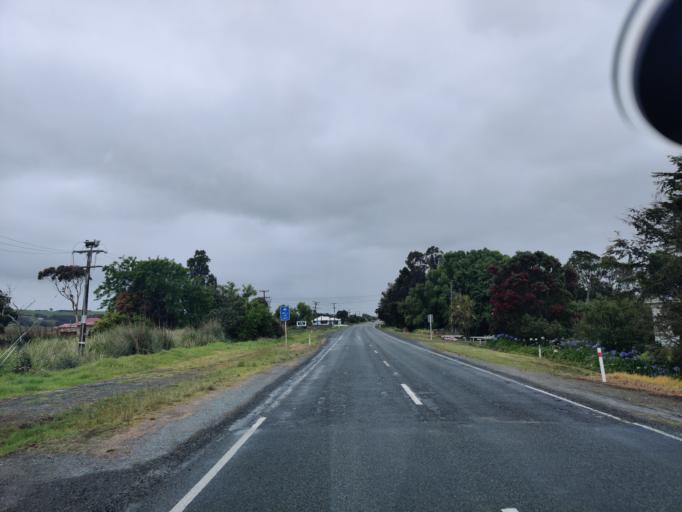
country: NZ
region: Northland
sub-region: Kaipara District
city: Dargaville
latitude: -35.9416
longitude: 173.8857
